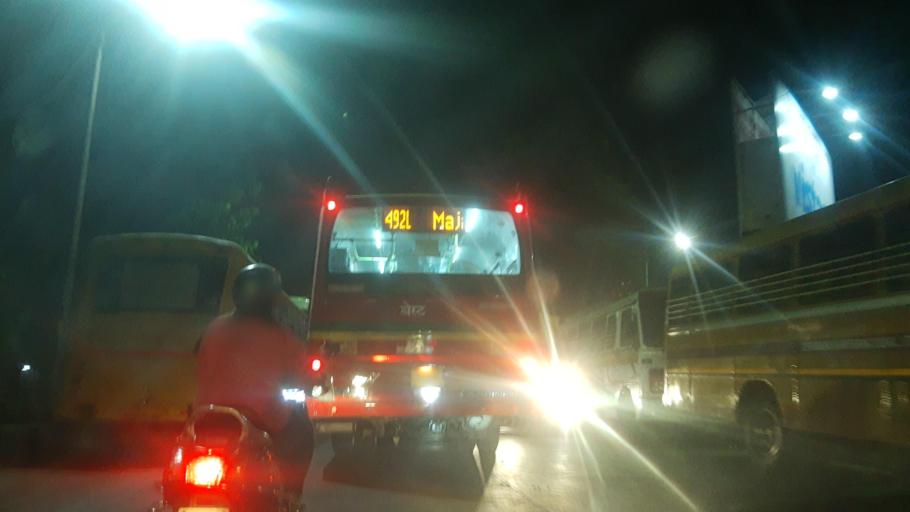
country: IN
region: Maharashtra
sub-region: Thane
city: Thane
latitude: 19.1782
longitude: 72.9681
